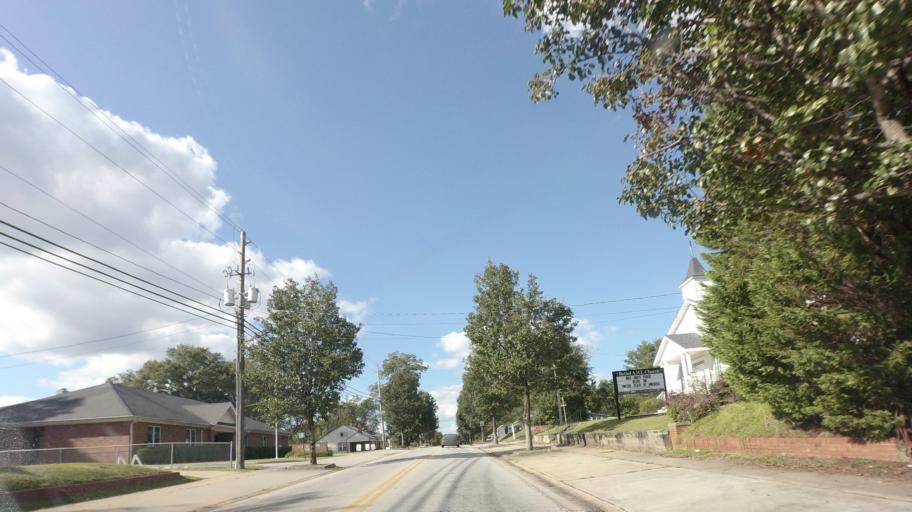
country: US
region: Georgia
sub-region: Lamar County
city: Barnesville
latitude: 33.0609
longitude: -84.1554
